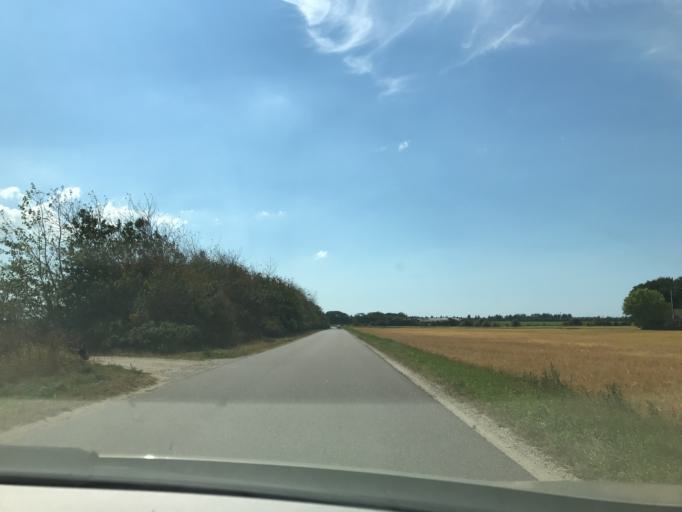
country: DK
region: Central Jutland
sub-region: Ringkobing-Skjern Kommune
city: Skjern
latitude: 55.8908
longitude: 8.4042
